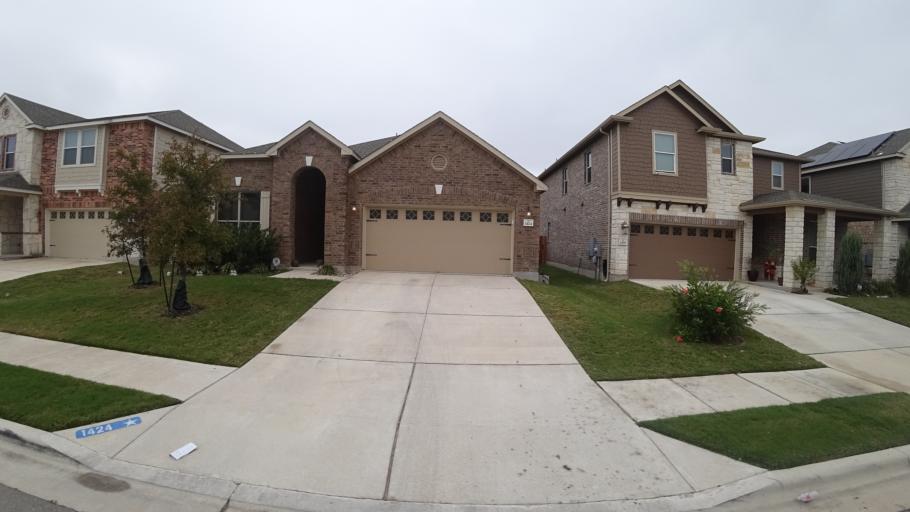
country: US
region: Texas
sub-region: Travis County
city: Pflugerville
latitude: 30.3953
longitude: -97.6486
